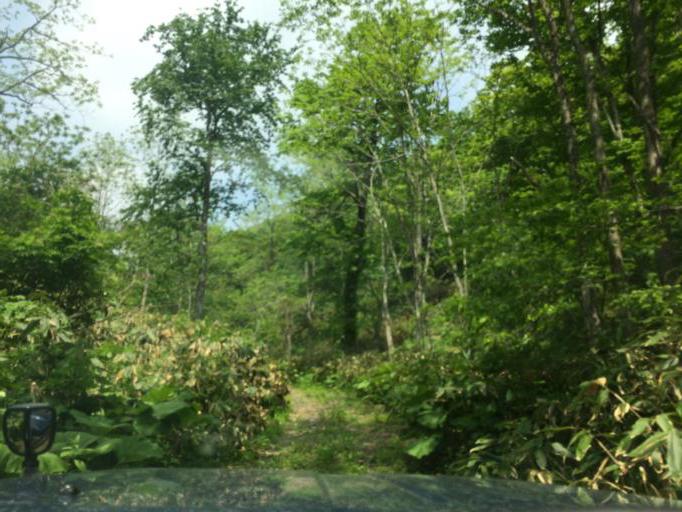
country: JP
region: Hokkaido
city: Niseko Town
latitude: 42.7155
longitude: 140.5434
